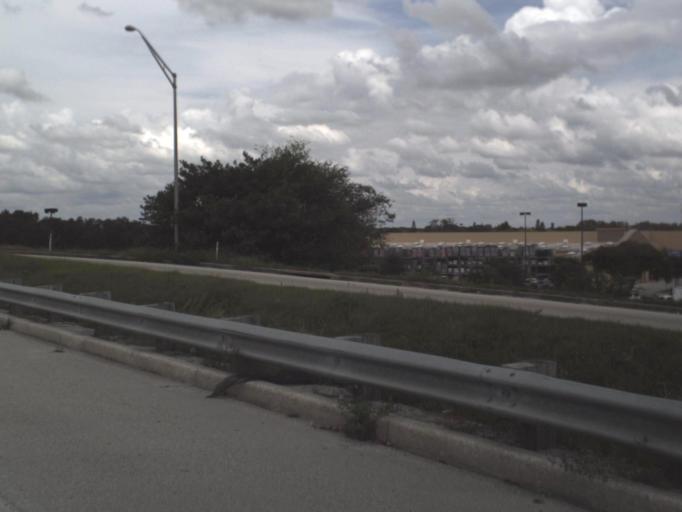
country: US
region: Florida
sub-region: Manatee County
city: Palmetto
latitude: 27.5227
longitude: -82.5619
